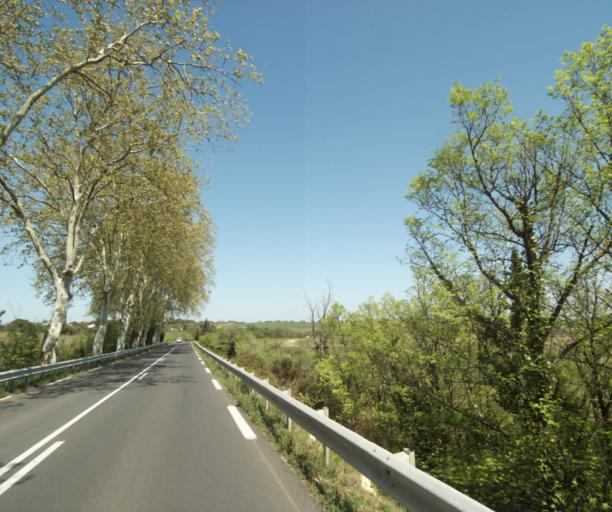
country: FR
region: Languedoc-Roussillon
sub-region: Departement de l'Herault
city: Restinclieres
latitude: 43.7121
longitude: 4.0287
